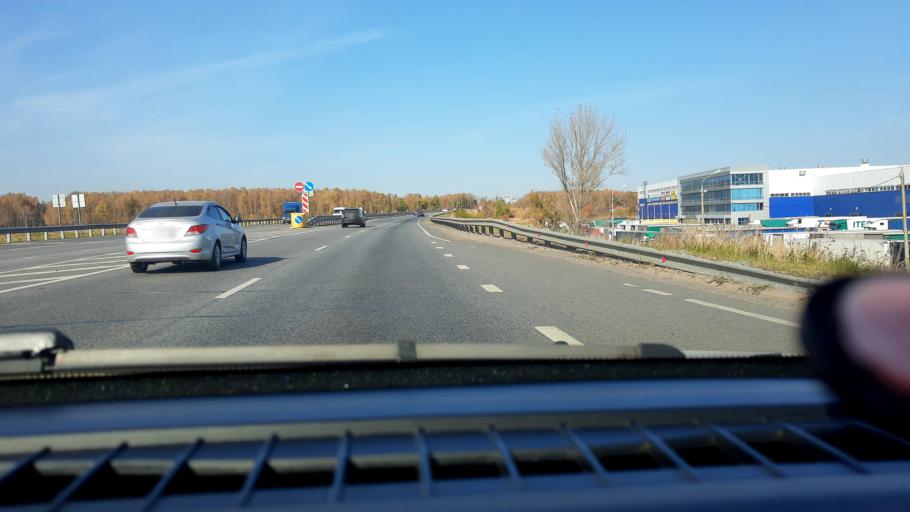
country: RU
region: Nizjnij Novgorod
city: Afonino
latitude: 56.2123
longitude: 44.0819
